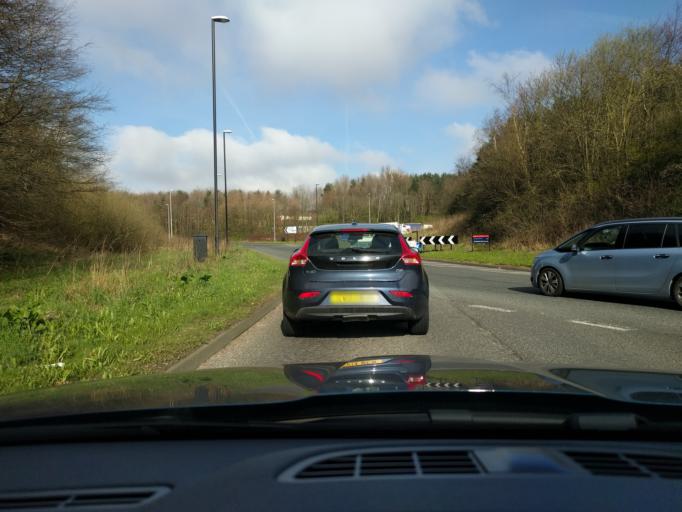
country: GB
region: England
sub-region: Sunderland
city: Washington
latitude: 54.8874
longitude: -1.5314
